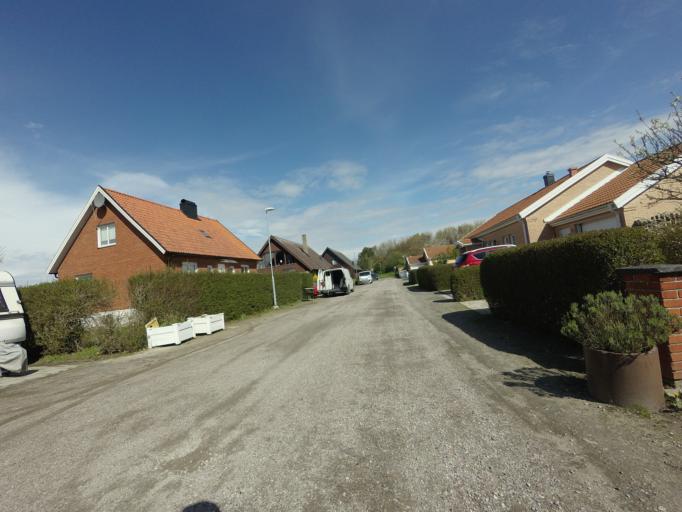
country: SE
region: Skane
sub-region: Malmo
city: Tygelsjo
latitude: 55.4947
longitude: 13.0014
